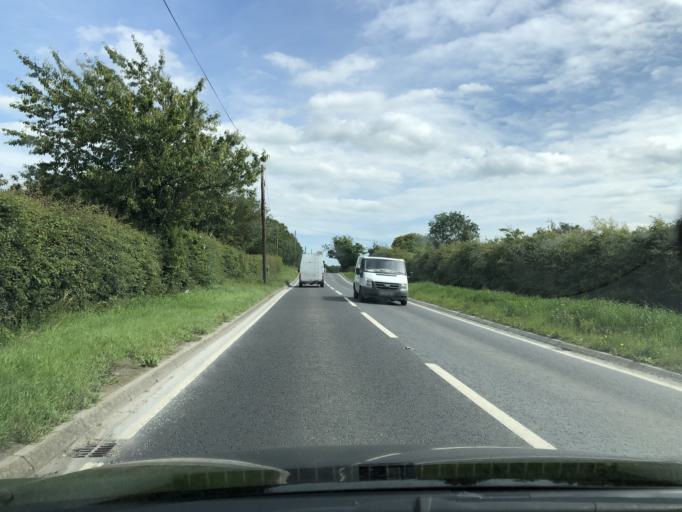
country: GB
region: Northern Ireland
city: Ballynahinch
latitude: 54.4196
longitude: -5.9135
